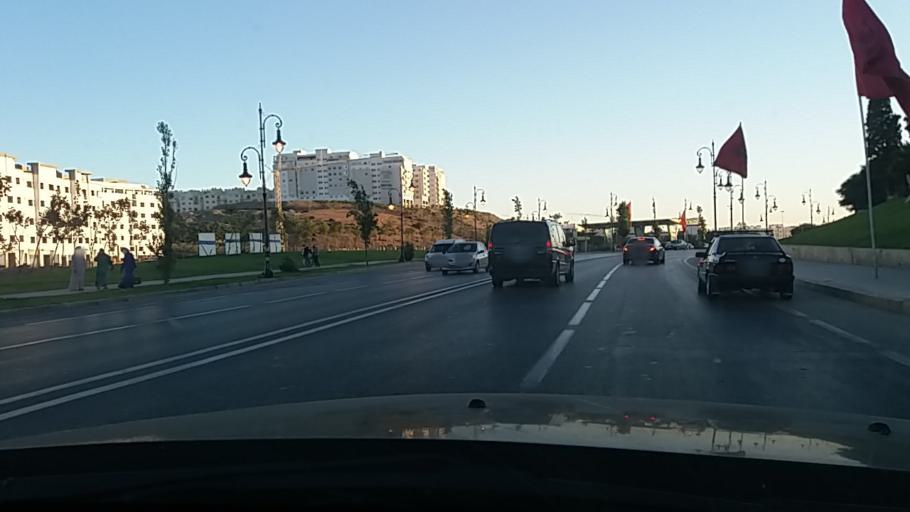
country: MA
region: Tanger-Tetouan
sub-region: Tanger-Assilah
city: Boukhalef
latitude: 35.7403
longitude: -5.8700
